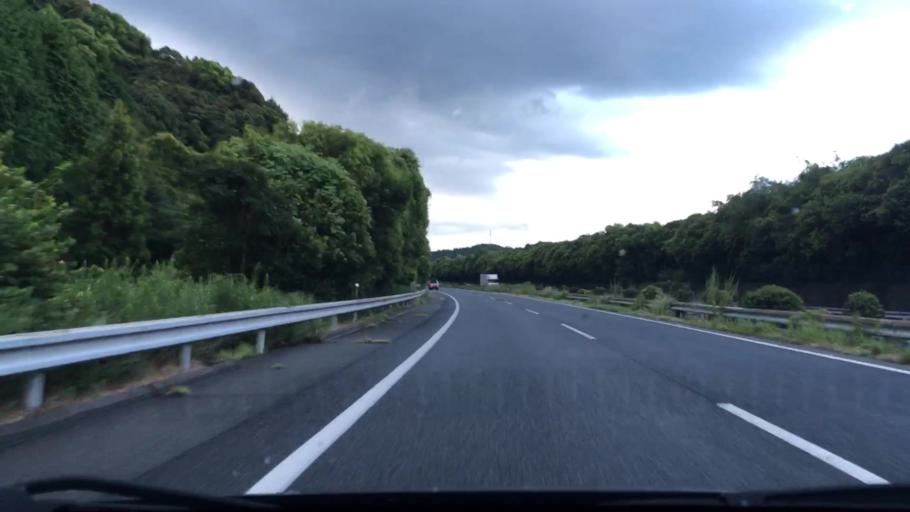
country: JP
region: Yamaguchi
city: Shimonoseki
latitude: 33.8773
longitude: 130.9693
